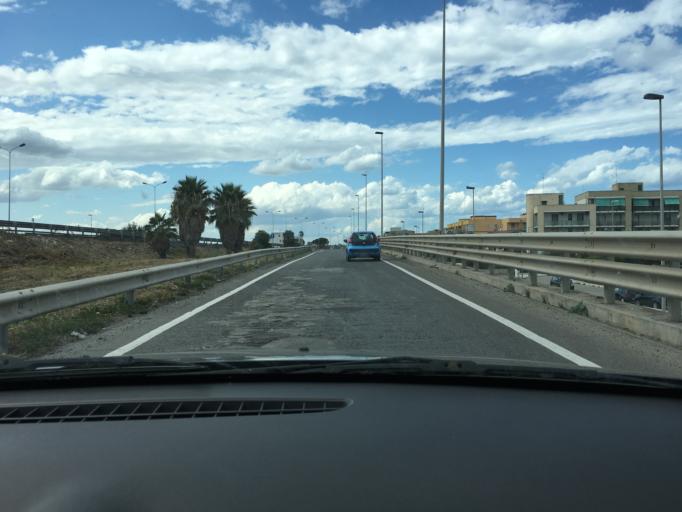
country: IT
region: Apulia
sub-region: Provincia di Bari
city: San Paolo
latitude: 41.1353
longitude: 16.8146
